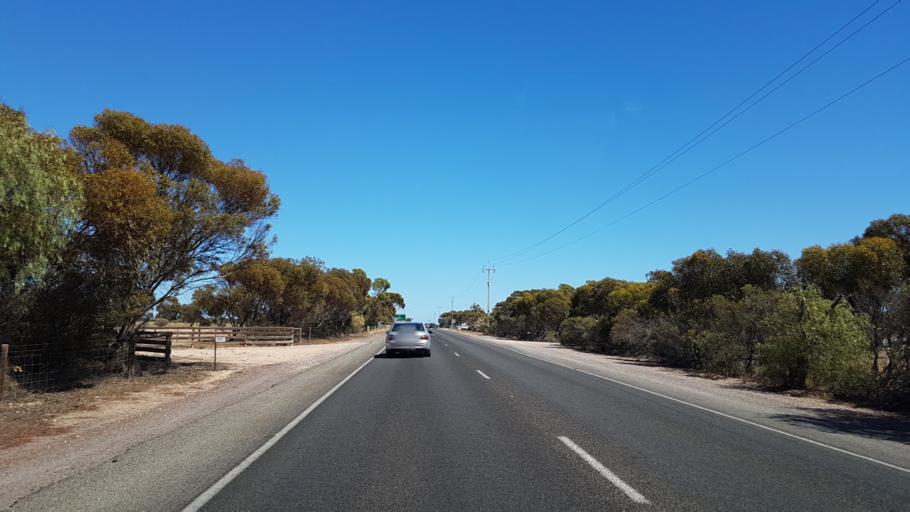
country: AU
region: South Australia
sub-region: Copper Coast
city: Wallaroo
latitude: -33.9425
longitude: 137.6566
